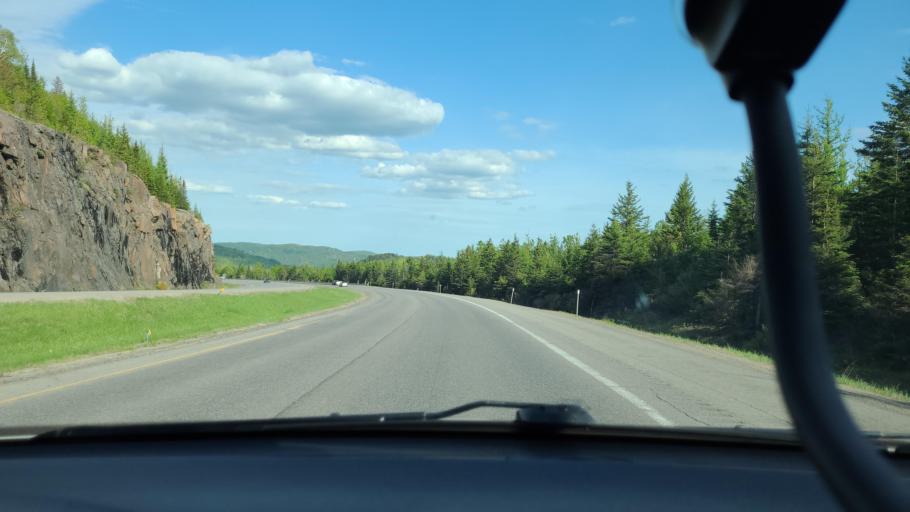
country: CA
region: Quebec
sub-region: Laurentides
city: Sainte-Adele
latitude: 45.9811
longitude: -74.1797
